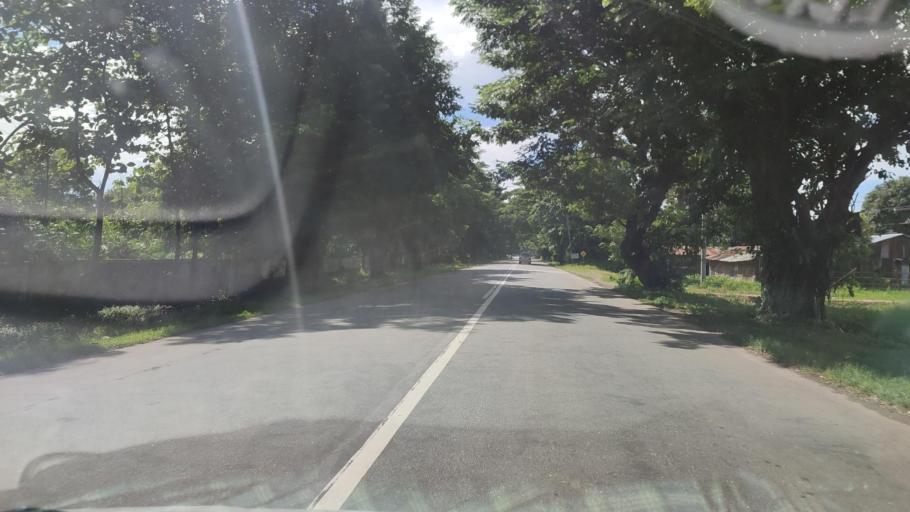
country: MM
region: Bago
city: Pyu
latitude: 18.2419
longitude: 96.5430
